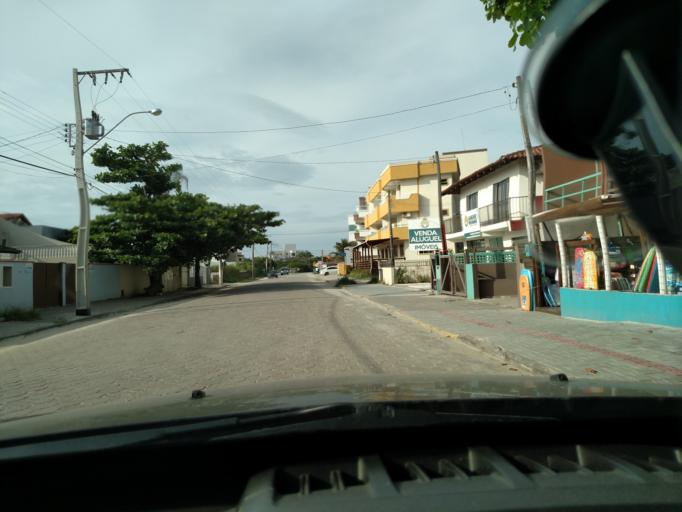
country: BR
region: Santa Catarina
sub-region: Porto Belo
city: Porto Belo
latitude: -27.1715
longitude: -48.4998
